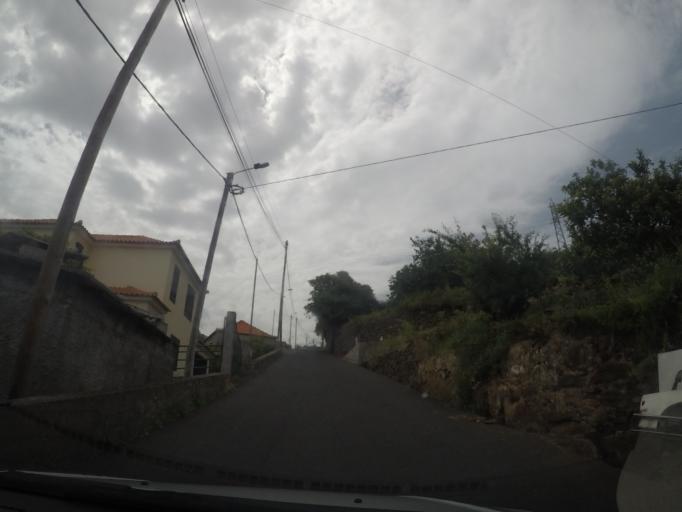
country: PT
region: Madeira
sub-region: Santa Cruz
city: Santa Cruz
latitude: 32.6883
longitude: -16.8097
